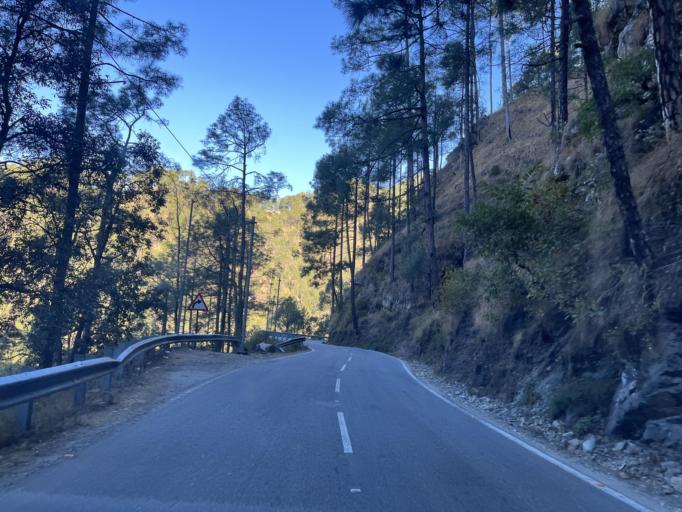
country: IN
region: Uttarakhand
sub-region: Naini Tal
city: Bhowali
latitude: 29.4026
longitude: 79.5106
